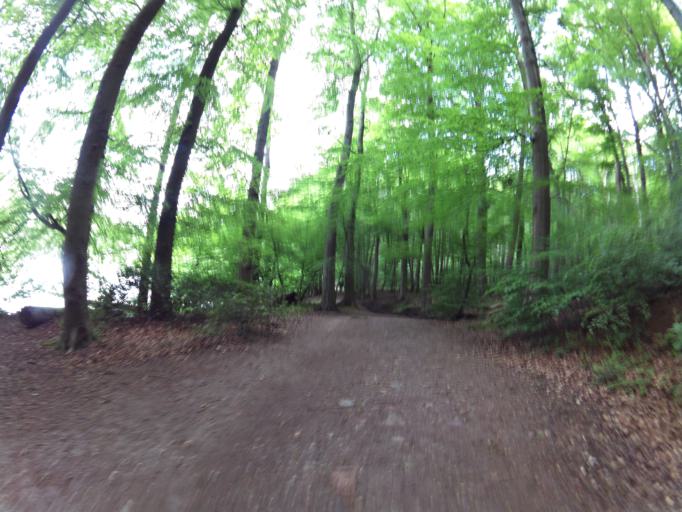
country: NL
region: Limburg
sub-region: Gemeente Kerkrade
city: Kerkrade
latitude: 50.8763
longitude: 6.0535
